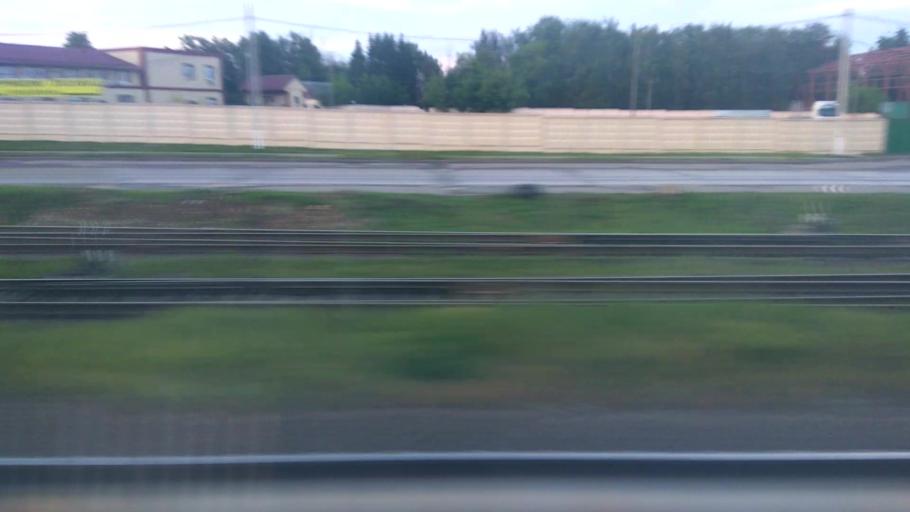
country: RU
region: Moskovskaya
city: Domodedovo
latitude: 55.4490
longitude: 37.7665
